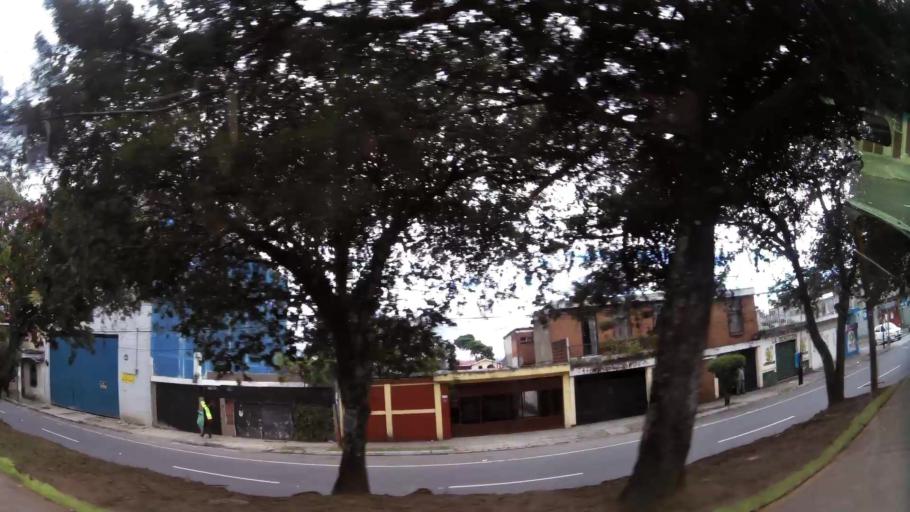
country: GT
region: Guatemala
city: Guatemala City
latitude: 14.6285
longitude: -90.5533
